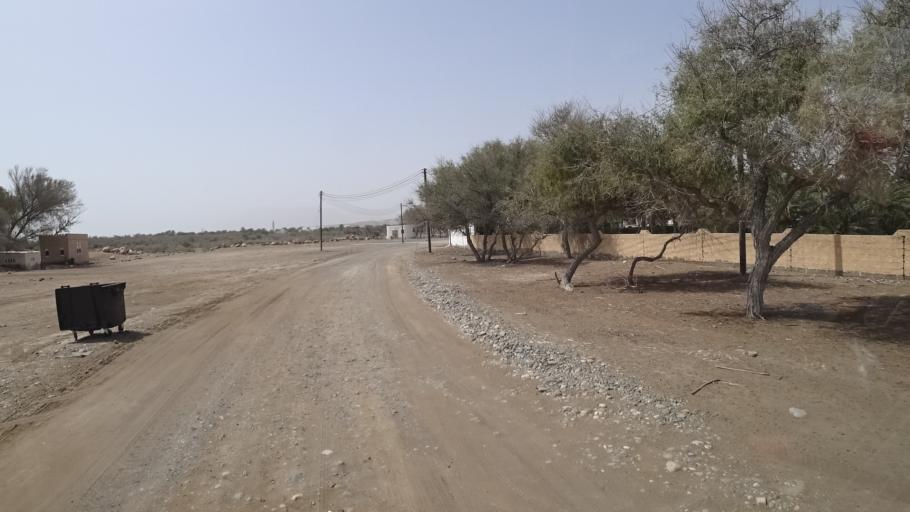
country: OM
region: Muhafazat Masqat
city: Muscat
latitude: 23.2180
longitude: 58.9745
